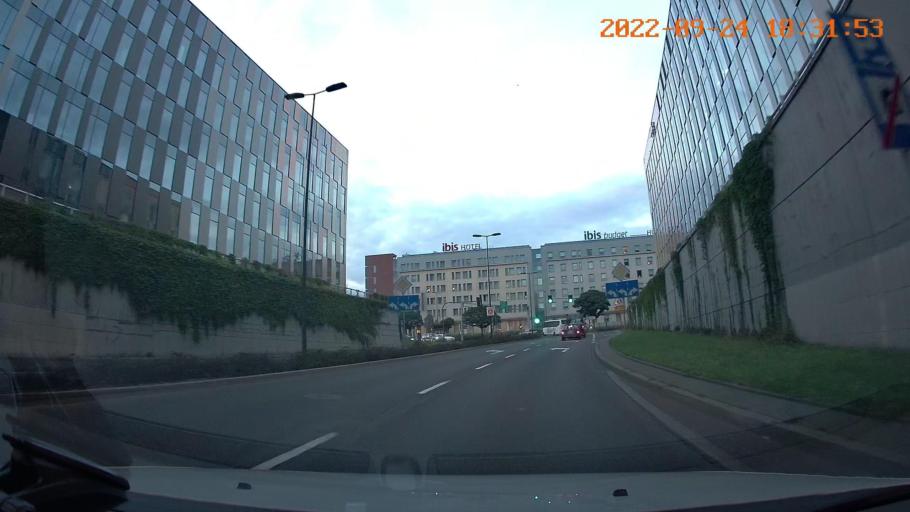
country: NG
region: Kwara
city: Kaiama
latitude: 10.0139
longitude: 3.9892
